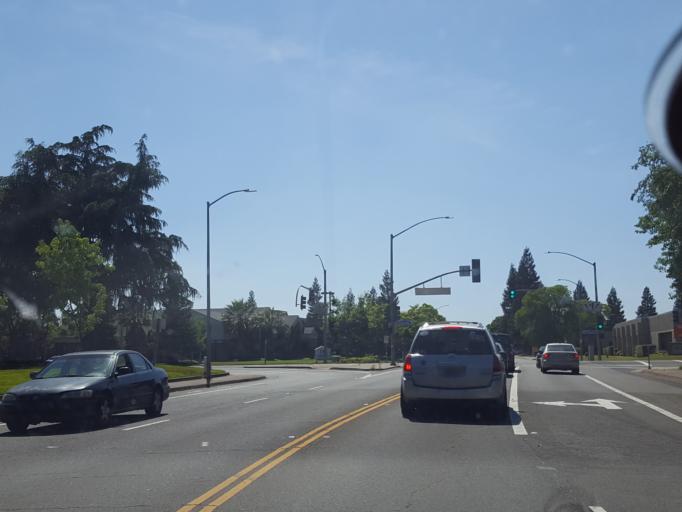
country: US
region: California
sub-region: Sacramento County
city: Rancho Cordova
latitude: 38.5741
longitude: -121.3060
